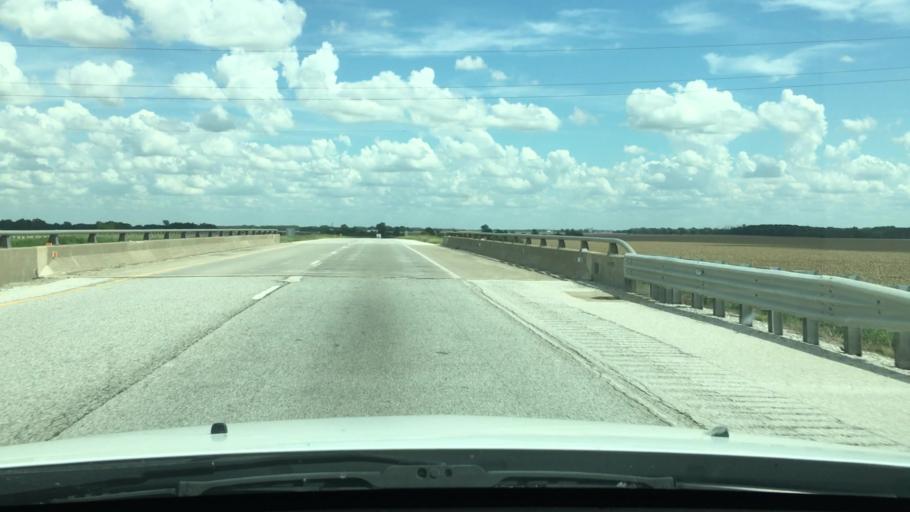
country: US
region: Illinois
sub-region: Morgan County
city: South Jacksonville
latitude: 39.6864
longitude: -90.2195
